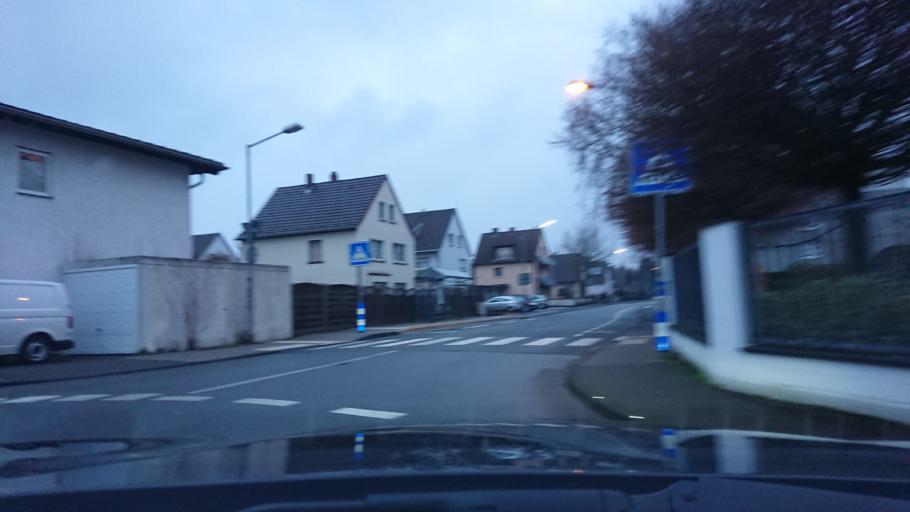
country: DE
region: North Rhine-Westphalia
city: Niederkassel
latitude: 50.8130
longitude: 7.0411
